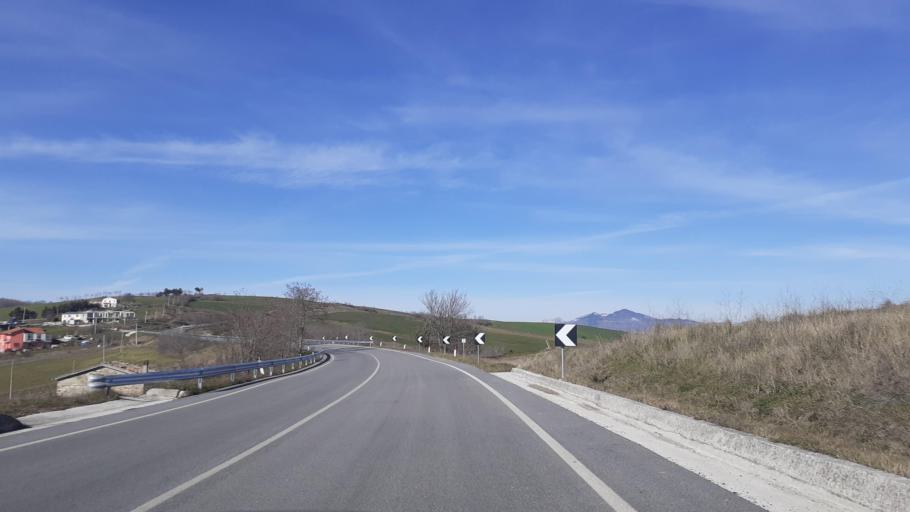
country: IT
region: Molise
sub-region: Provincia di Campobasso
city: Pietracupa
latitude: 41.6845
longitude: 14.5136
